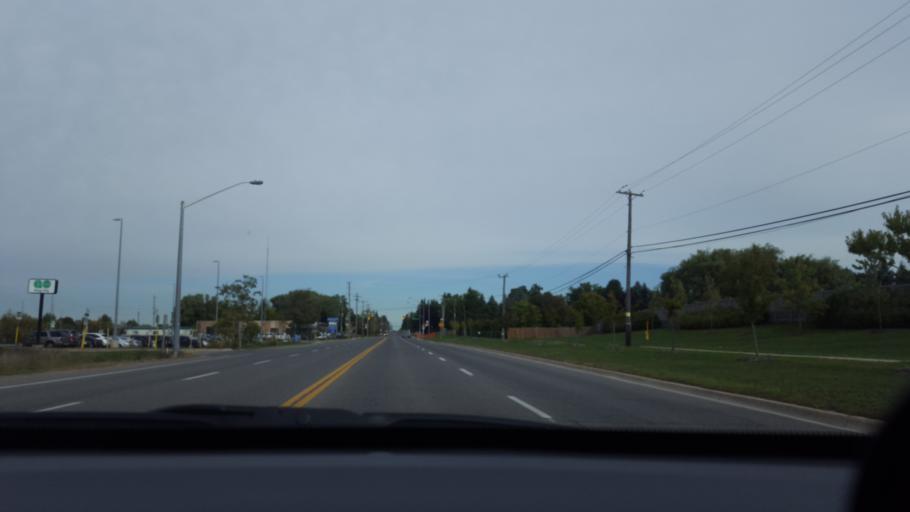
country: CA
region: Ontario
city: Vaughan
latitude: 43.9191
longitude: -79.5256
